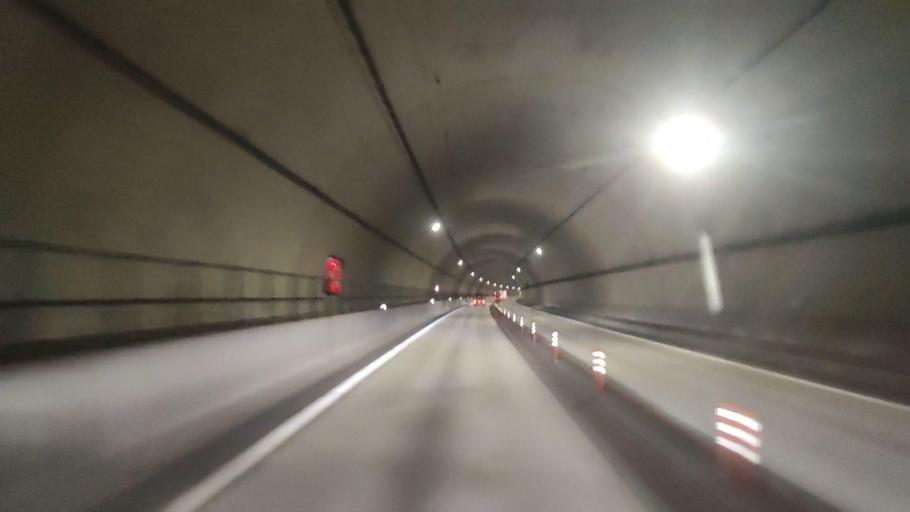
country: JP
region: Wakayama
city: Tanabe
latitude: 33.5906
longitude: 135.4399
